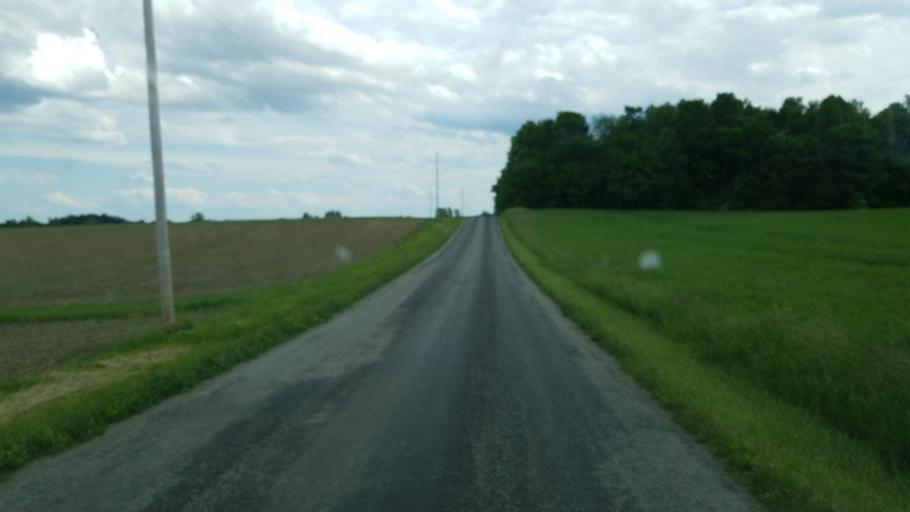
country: US
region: Ohio
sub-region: Richland County
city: Shelby
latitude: 40.9331
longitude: -82.5712
